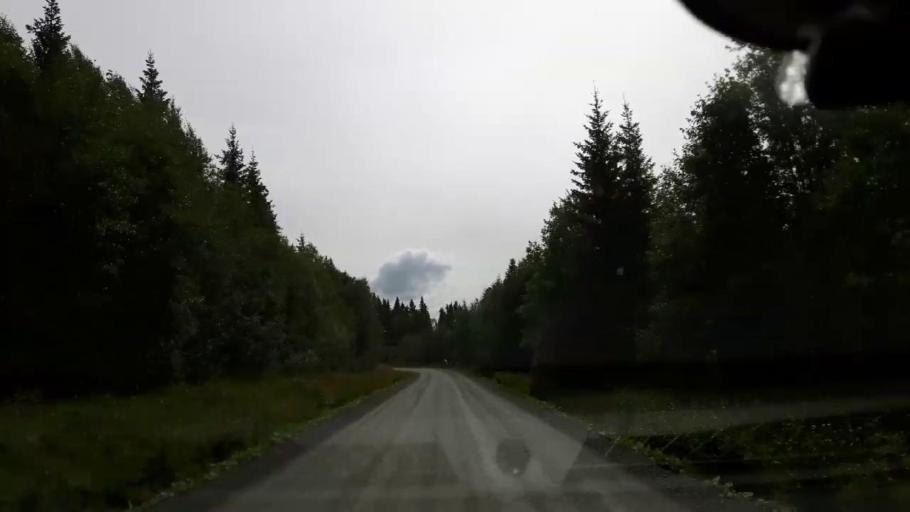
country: SE
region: Jaemtland
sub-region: Krokoms Kommun
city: Valla
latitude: 63.6309
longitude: 14.0197
